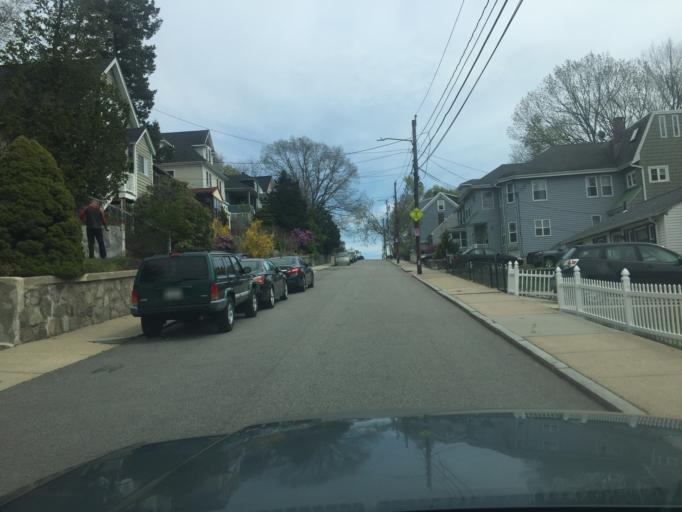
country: US
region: Massachusetts
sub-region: Suffolk County
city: Jamaica Plain
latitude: 42.2778
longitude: -71.1315
